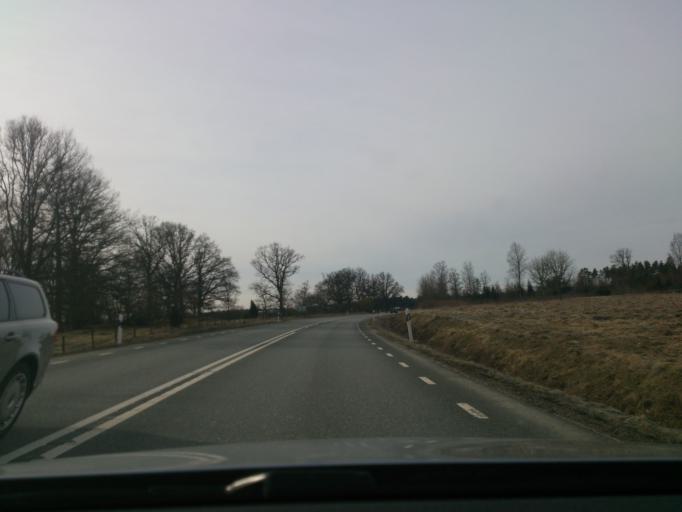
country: SE
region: Kronoberg
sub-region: Alvesta Kommun
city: Moheda
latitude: 56.9587
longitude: 14.5720
